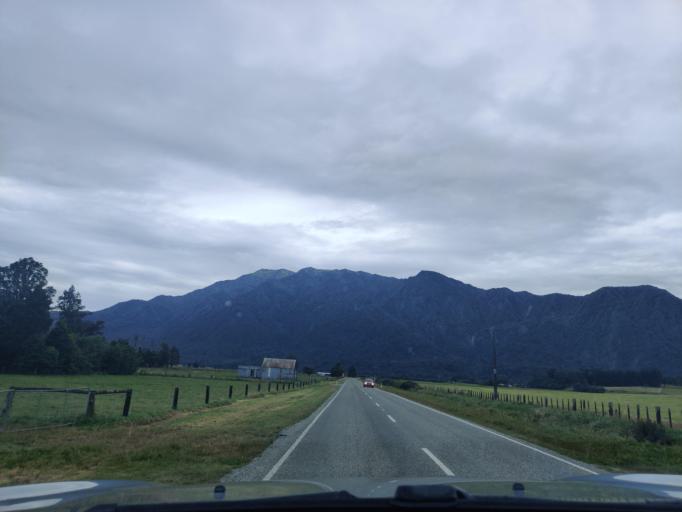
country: NZ
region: West Coast
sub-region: Westland District
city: Hokitika
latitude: -43.1534
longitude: 170.6034
